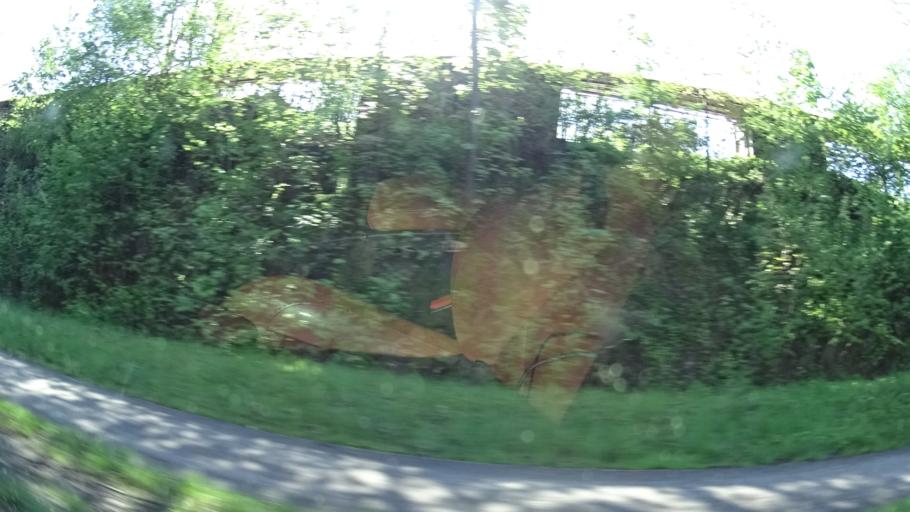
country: DE
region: Baden-Wuerttemberg
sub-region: Karlsruhe Region
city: Rohrdorf
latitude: 48.5628
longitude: 8.6979
